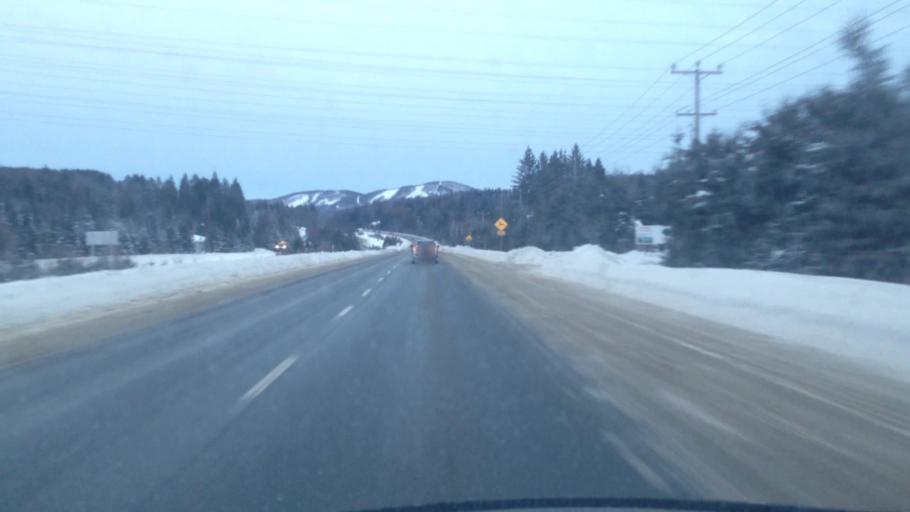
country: CA
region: Quebec
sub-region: Laurentides
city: Mont-Tremblant
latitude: 46.1151
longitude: -74.5481
